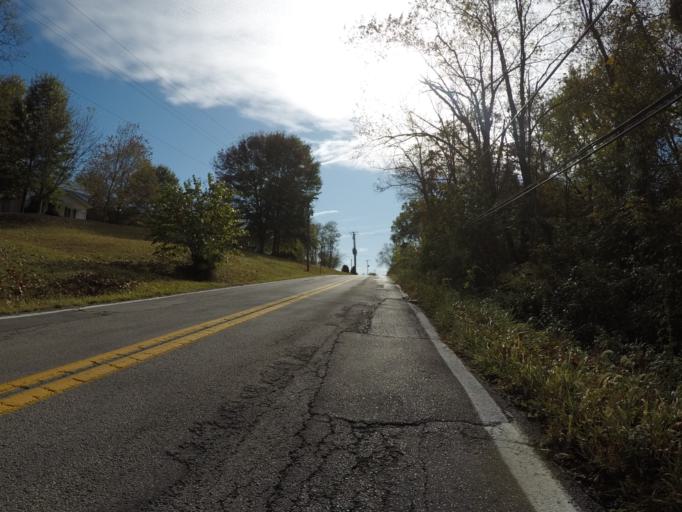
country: US
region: West Virginia
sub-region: Wayne County
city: Ceredo
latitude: 38.3616
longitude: -82.5290
